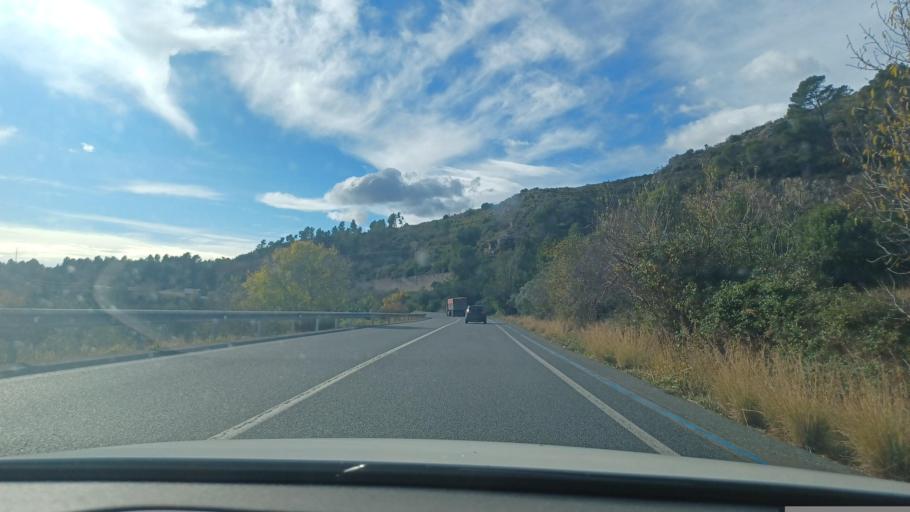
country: ES
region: Catalonia
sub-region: Provincia de Tarragona
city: Alcover
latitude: 41.2947
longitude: 1.1908
